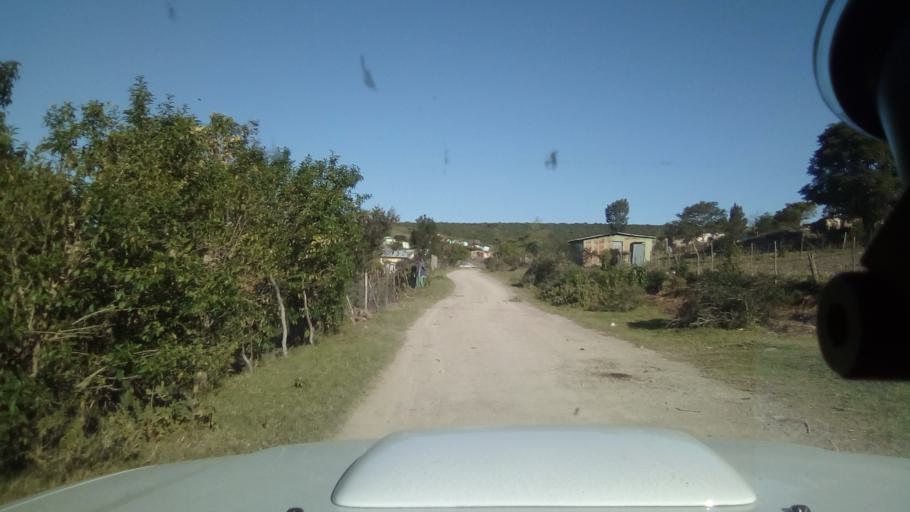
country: ZA
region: Eastern Cape
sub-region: Buffalo City Metropolitan Municipality
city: Bhisho
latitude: -32.8027
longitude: 27.3409
